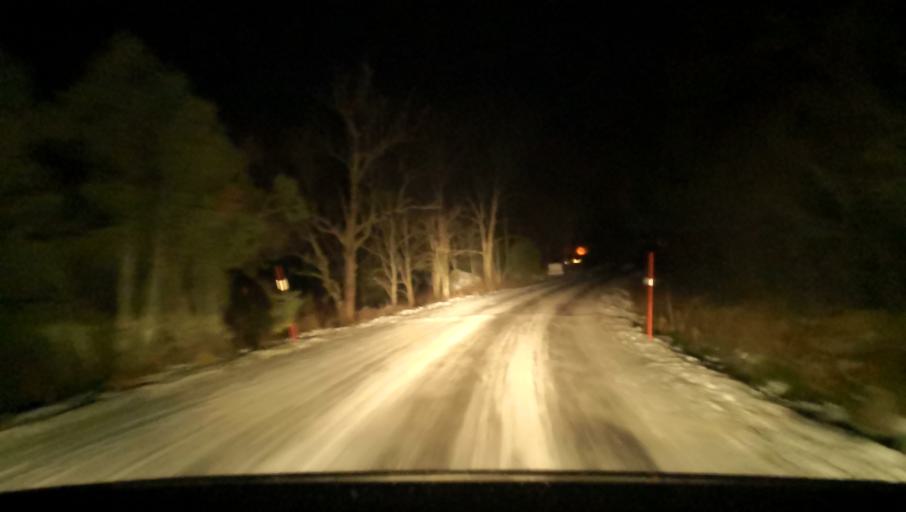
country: SE
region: Uppsala
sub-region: Enkopings Kommun
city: Hummelsta
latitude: 59.6268
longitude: 16.8855
